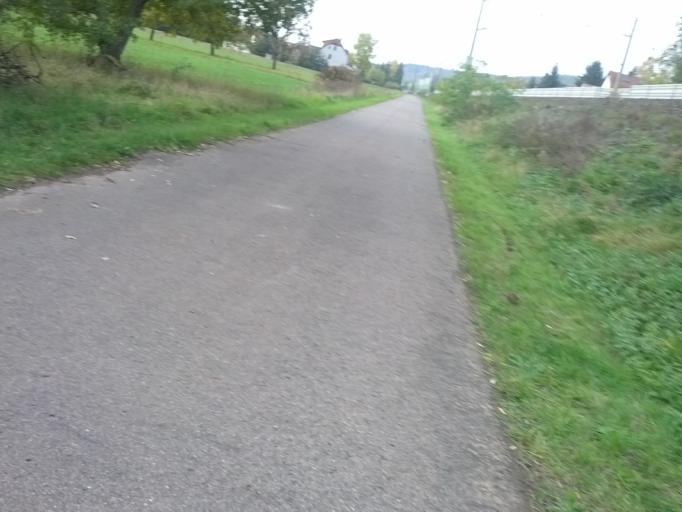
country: DE
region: Thuringia
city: Thal
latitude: 50.9603
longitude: 10.3874
